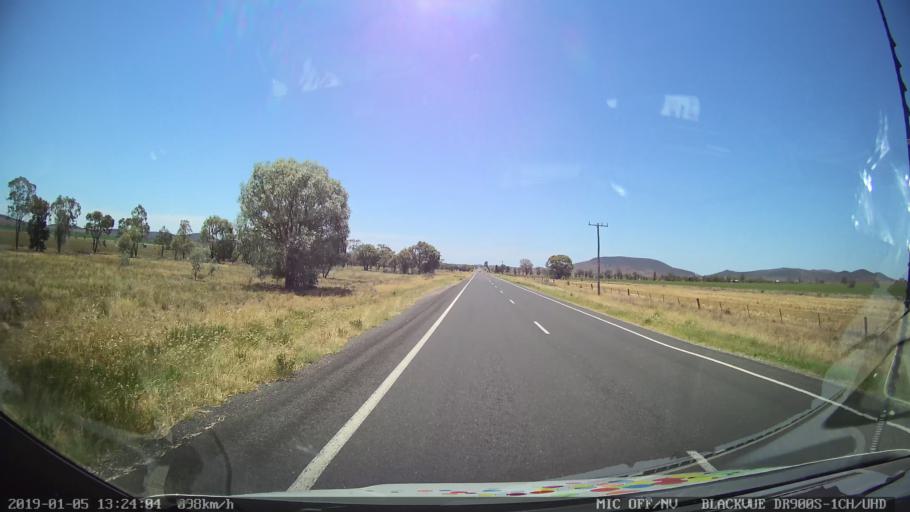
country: AU
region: New South Wales
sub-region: Gunnedah
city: Gunnedah
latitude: -31.0727
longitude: 149.9838
